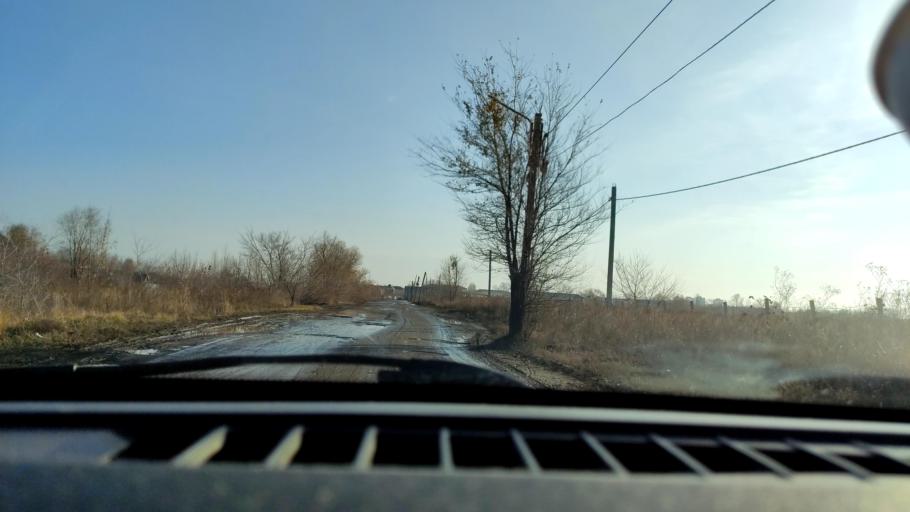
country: RU
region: Samara
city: Samara
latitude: 53.1187
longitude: 50.1067
